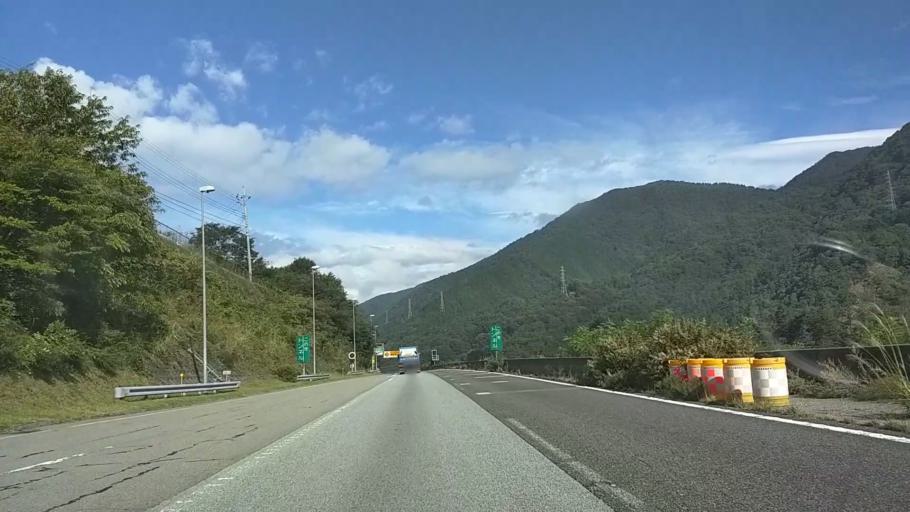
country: JP
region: Yamanashi
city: Enzan
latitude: 35.6373
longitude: 138.7761
